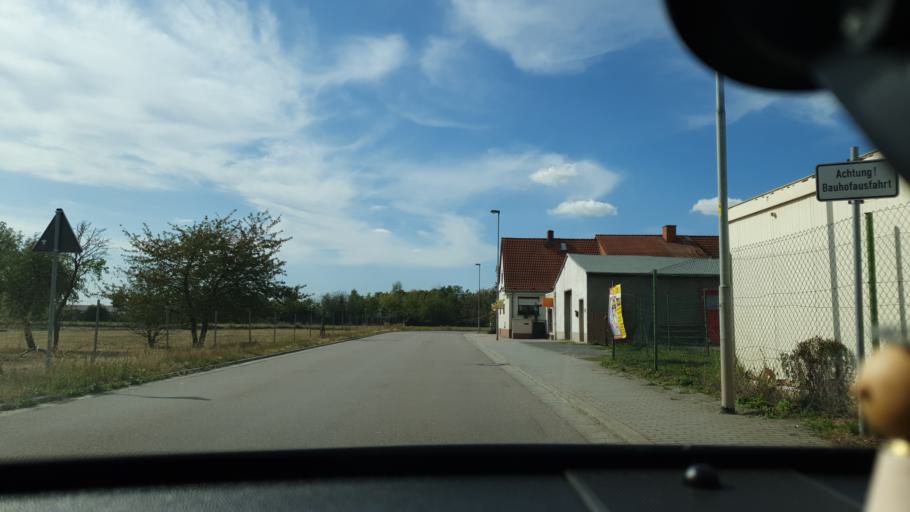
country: DE
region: Saxony
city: Krostitz
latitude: 51.4579
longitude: 12.4543
